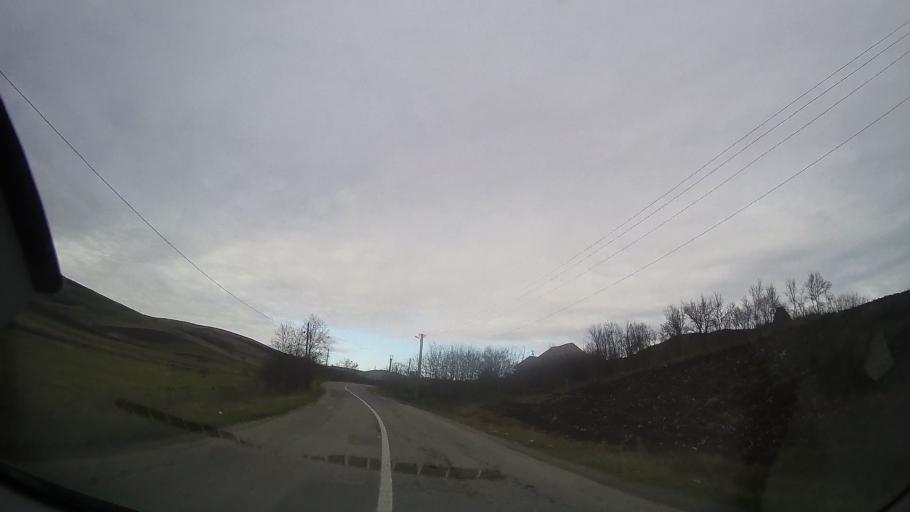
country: RO
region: Cluj
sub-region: Comuna Camarasu
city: Camarasu
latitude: 46.8068
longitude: 24.1451
